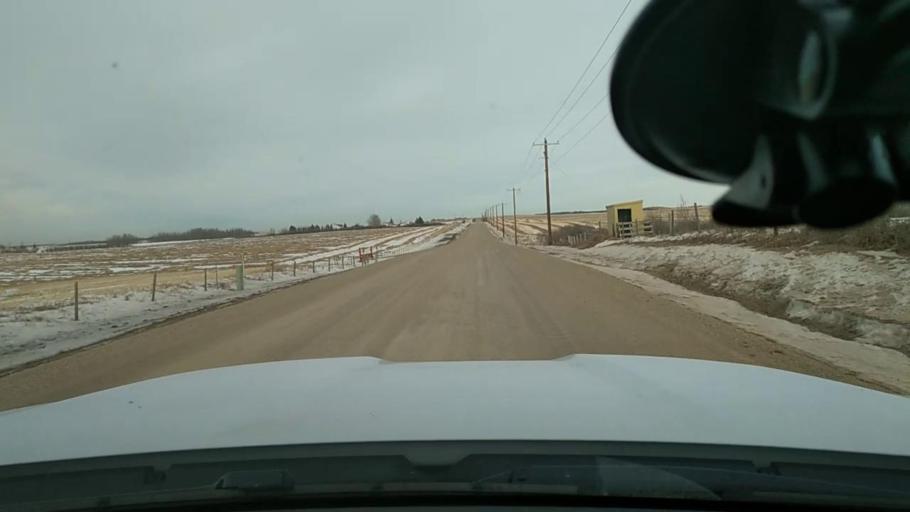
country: CA
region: Alberta
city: Airdrie
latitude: 51.2264
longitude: -113.9118
